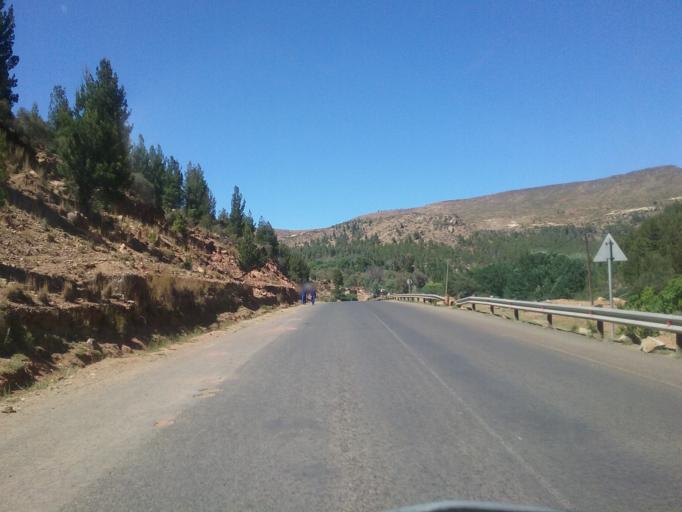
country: LS
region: Quthing
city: Quthing
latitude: -30.3997
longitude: 27.6860
